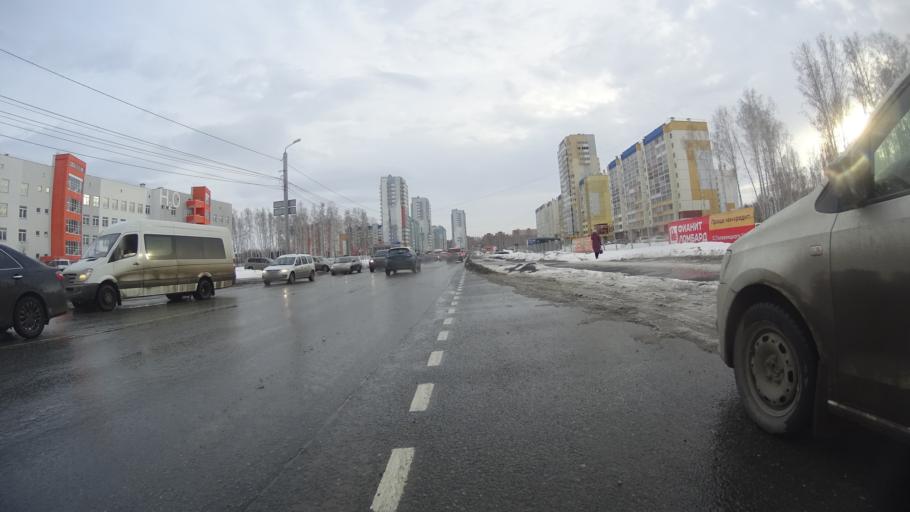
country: RU
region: Chelyabinsk
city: Roshchino
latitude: 55.2066
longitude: 61.2843
